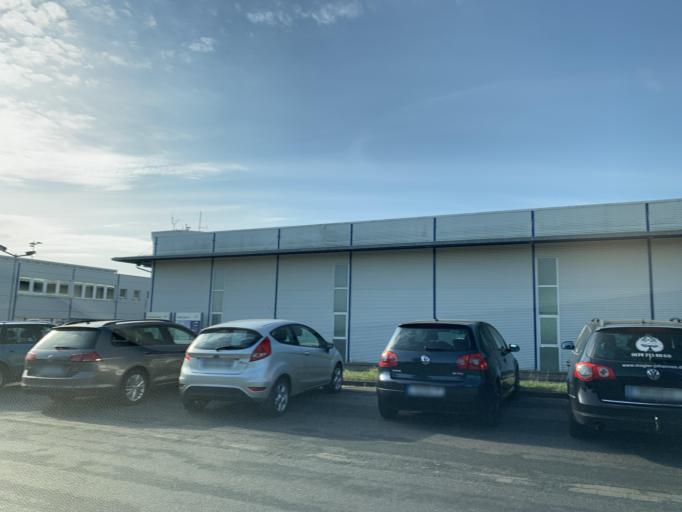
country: DE
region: Mecklenburg-Vorpommern
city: Trollenhagen
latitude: 53.6049
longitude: 13.2986
